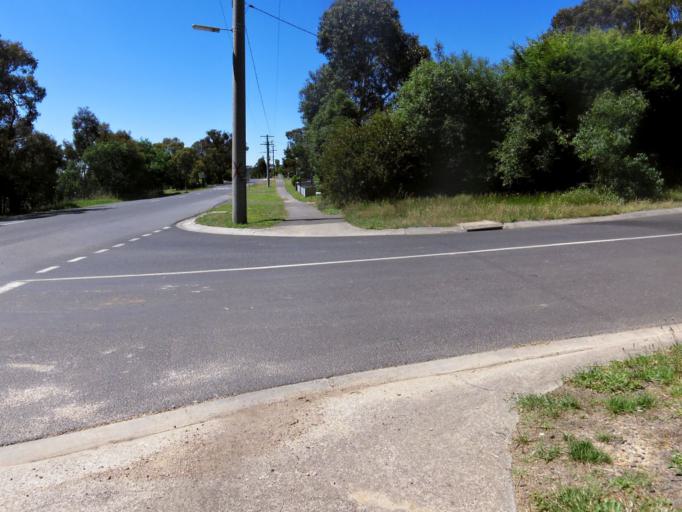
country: AU
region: Victoria
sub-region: Whittlesea
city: Whittlesea
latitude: -37.3621
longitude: 145.0272
